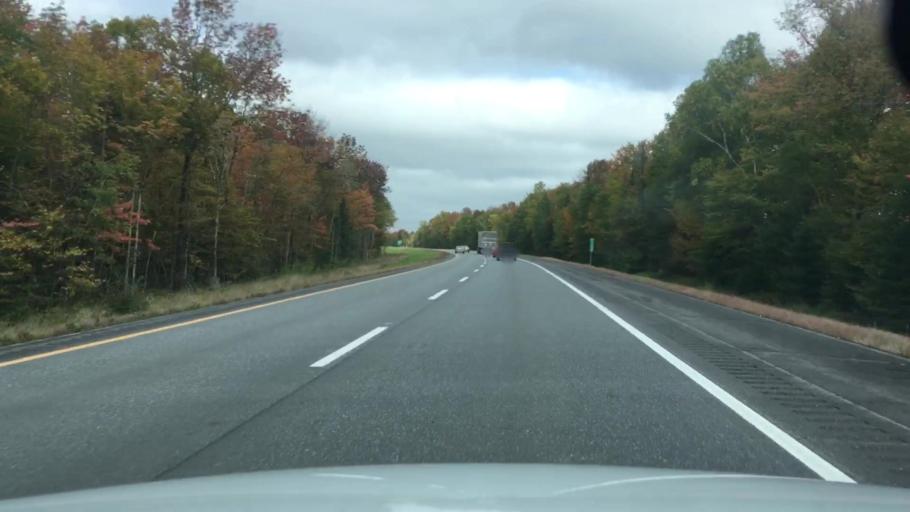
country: US
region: Maine
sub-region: Somerset County
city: Palmyra
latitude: 44.8154
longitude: -69.3385
